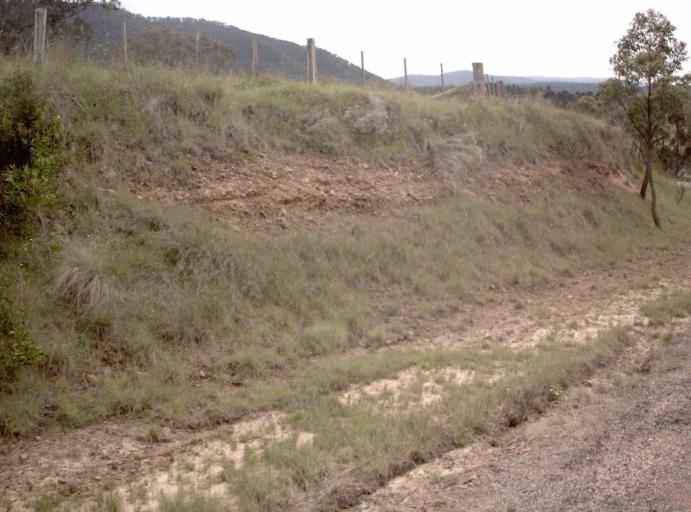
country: AU
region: Victoria
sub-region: East Gippsland
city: Bairnsdale
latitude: -37.5874
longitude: 147.1836
